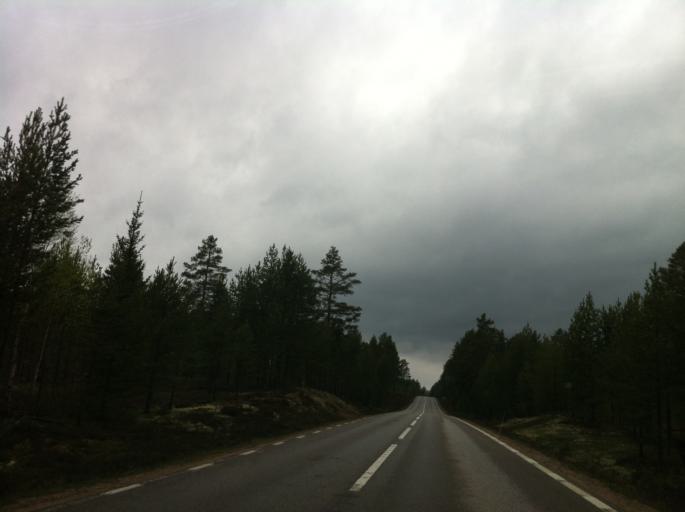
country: SE
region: Jaemtland
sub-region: Harjedalens Kommun
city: Sveg
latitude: 62.0283
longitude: 14.4258
